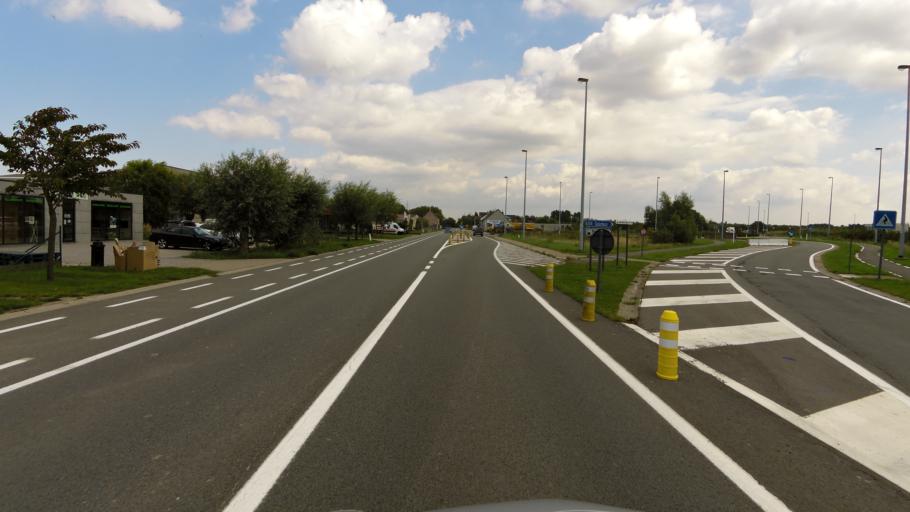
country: BE
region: Flanders
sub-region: Provincie West-Vlaanderen
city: Bredene
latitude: 51.2222
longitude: 2.9845
